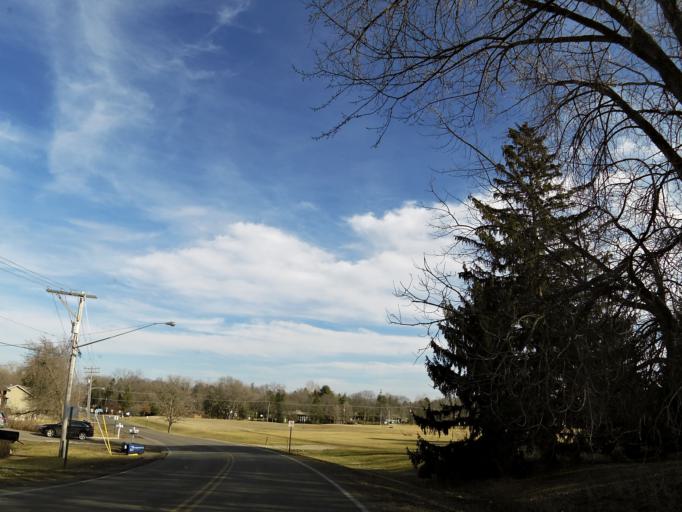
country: US
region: Minnesota
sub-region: Rice County
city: Northfield
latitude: 44.4641
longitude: -93.1788
